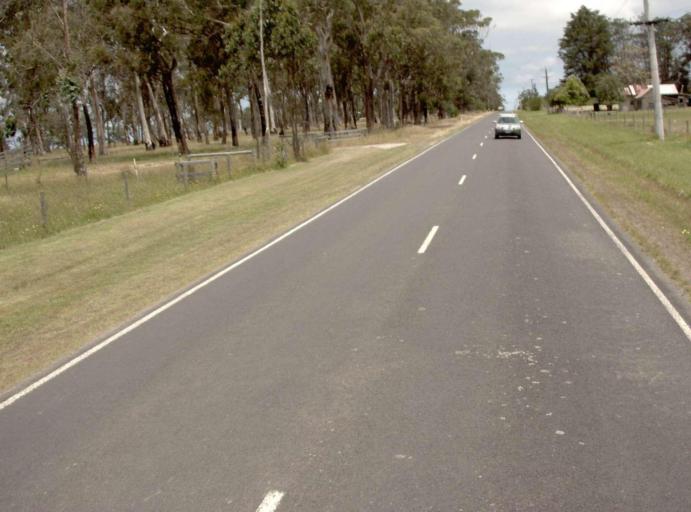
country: AU
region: Victoria
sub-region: Latrobe
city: Traralgon
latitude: -38.5320
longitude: 146.6584
